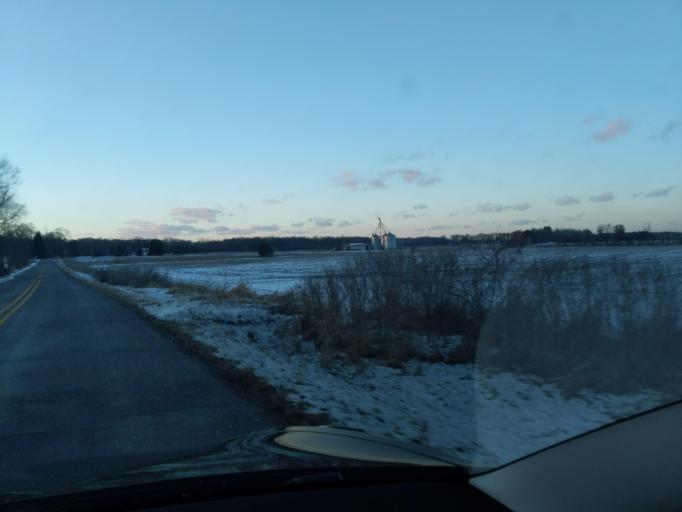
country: US
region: Michigan
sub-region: Ingham County
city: Stockbridge
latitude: 42.4687
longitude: -84.2847
